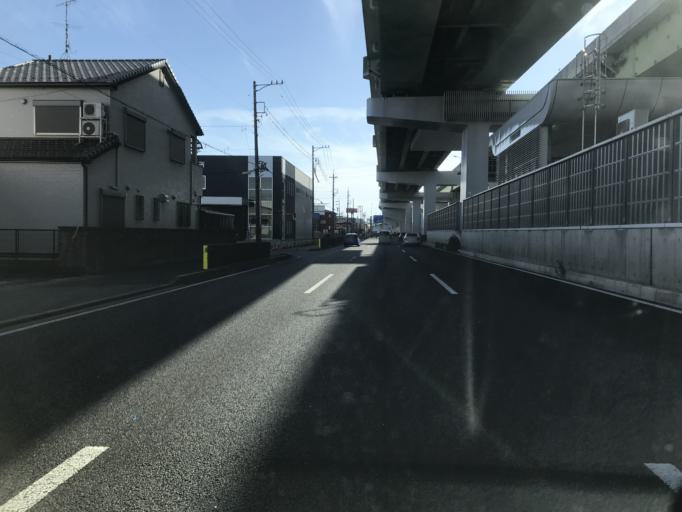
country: JP
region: Aichi
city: Iwakura
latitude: 35.2496
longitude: 136.8445
